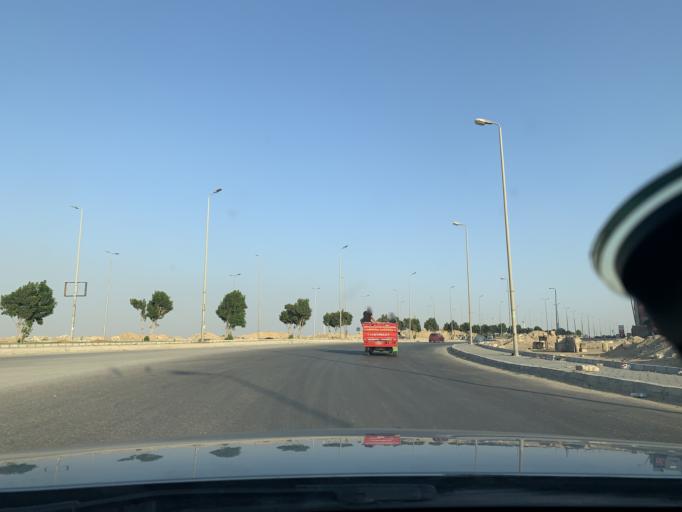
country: EG
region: Muhafazat al Qalyubiyah
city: Al Khankah
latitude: 30.0418
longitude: 31.5235
